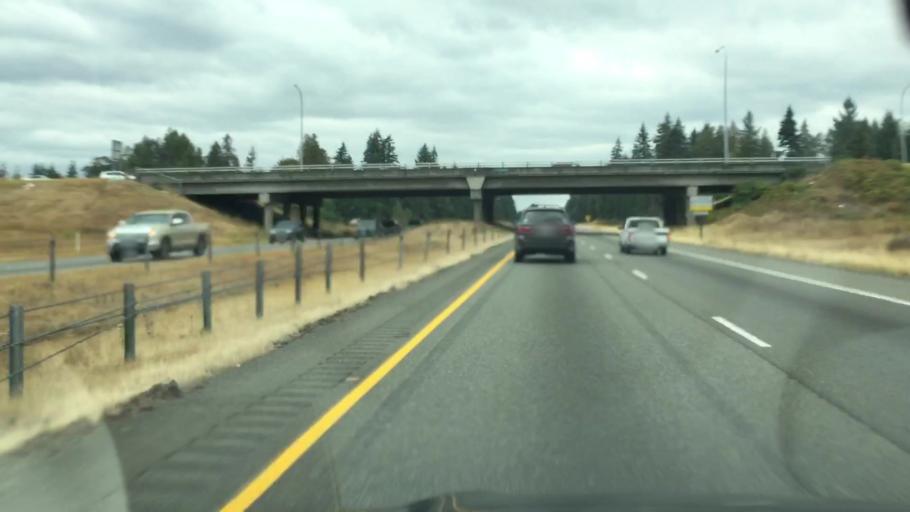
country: US
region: Washington
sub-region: Pierce County
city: Summit
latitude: 47.1581
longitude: -122.3559
